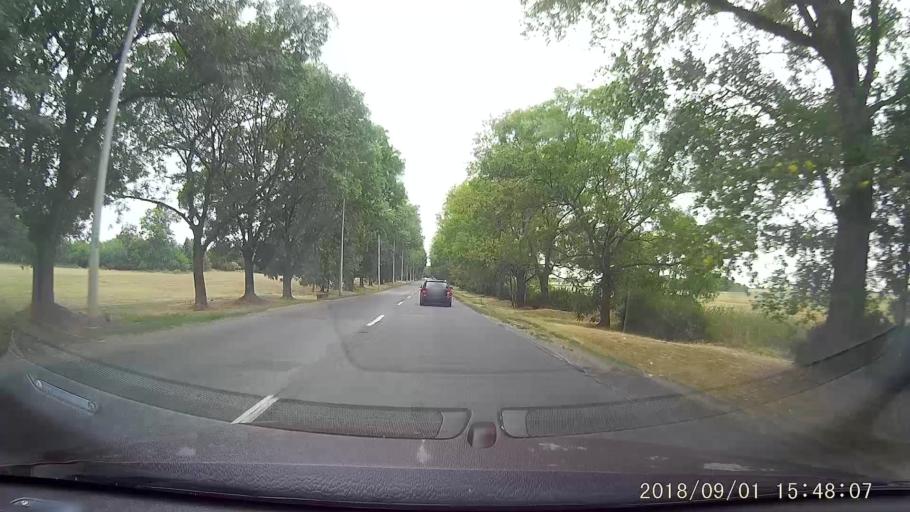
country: PL
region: Lubusz
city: Gorzow Wielkopolski
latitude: 52.7414
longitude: 15.1810
